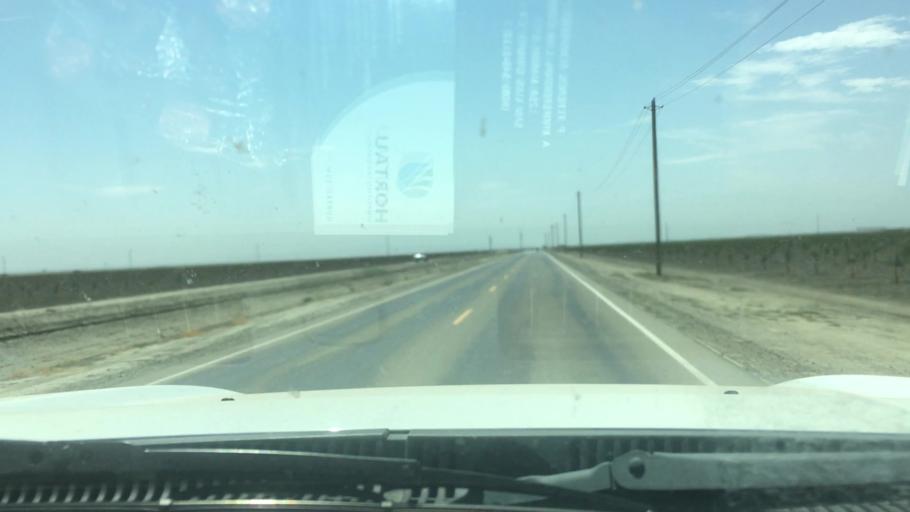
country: US
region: California
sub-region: Kings County
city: Corcoran
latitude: 36.0508
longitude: -119.5646
